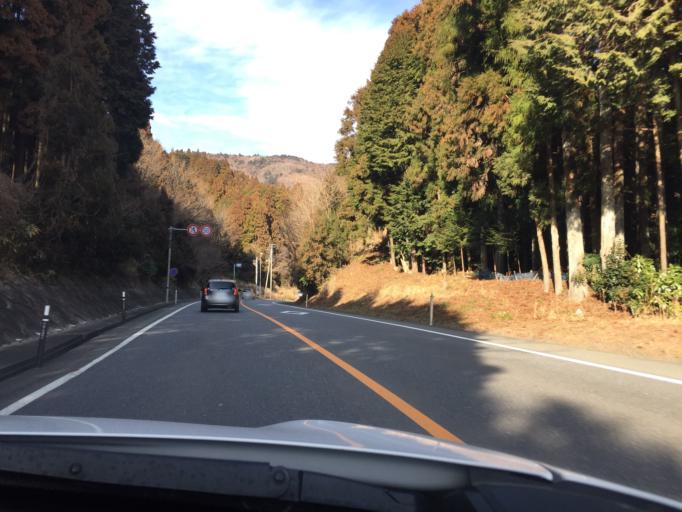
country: JP
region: Fukushima
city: Iwaki
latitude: 37.0791
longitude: 140.7991
